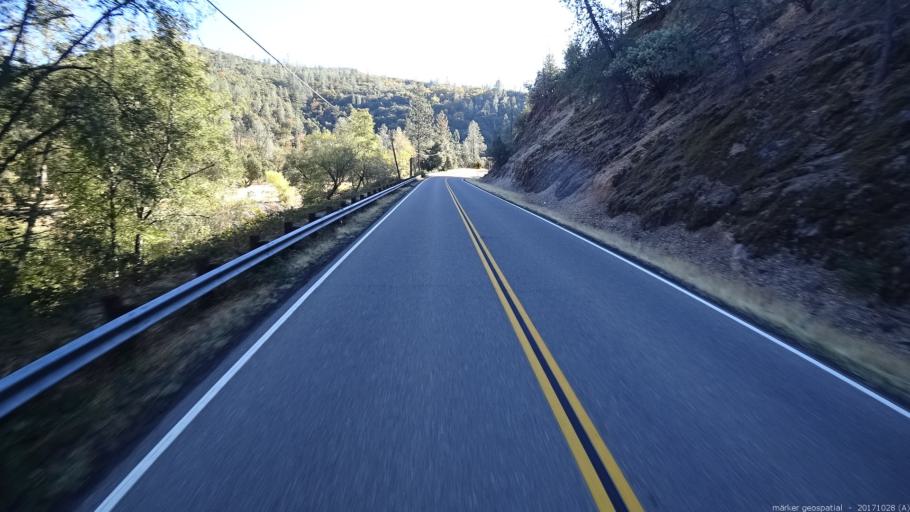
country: US
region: California
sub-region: Shasta County
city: Shasta
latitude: 40.6681
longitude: -122.6354
